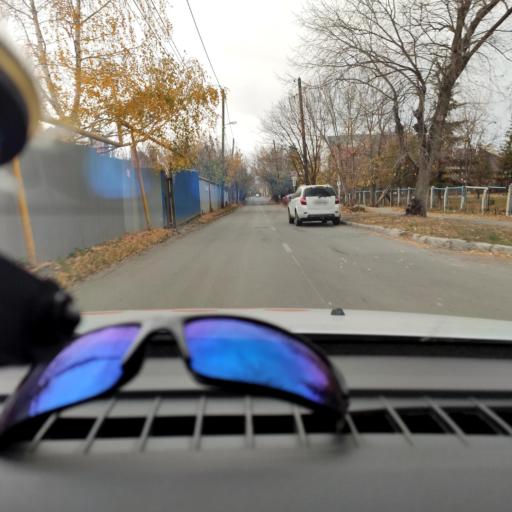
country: RU
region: Samara
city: Samara
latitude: 53.2346
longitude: 50.1778
